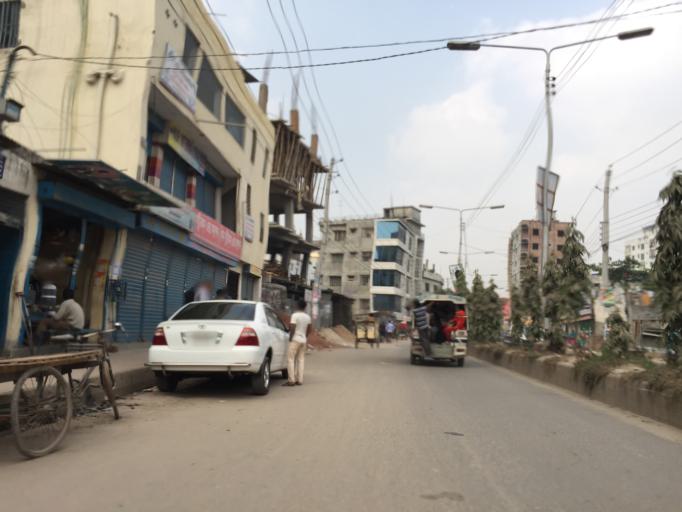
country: BD
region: Dhaka
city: Azimpur
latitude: 23.7858
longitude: 90.3672
